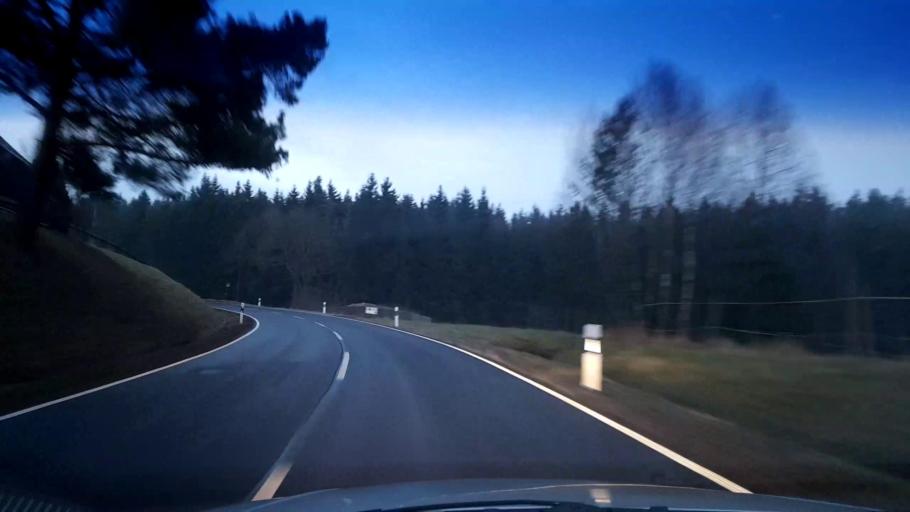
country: DE
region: Bavaria
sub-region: Upper Franconia
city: Arzberg
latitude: 50.0382
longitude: 12.2005
